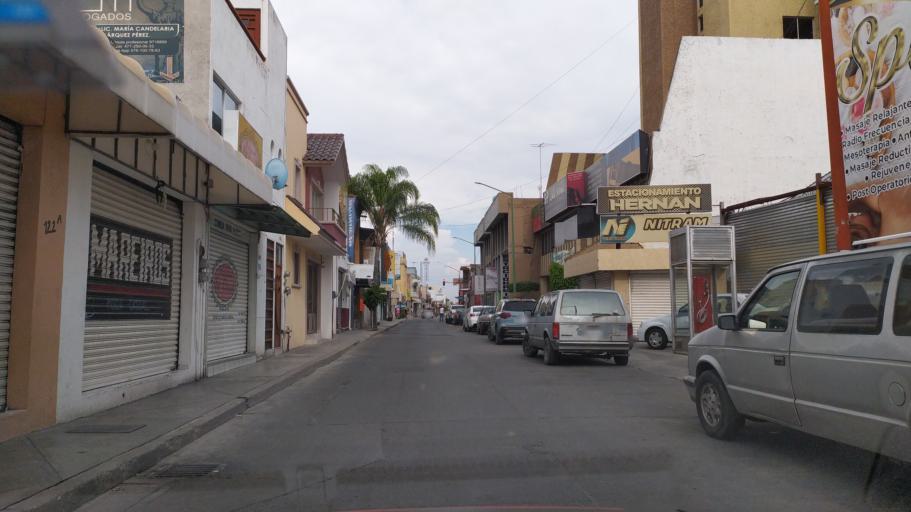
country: MX
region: Guanajuato
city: San Francisco del Rincon
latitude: 21.0171
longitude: -101.8592
